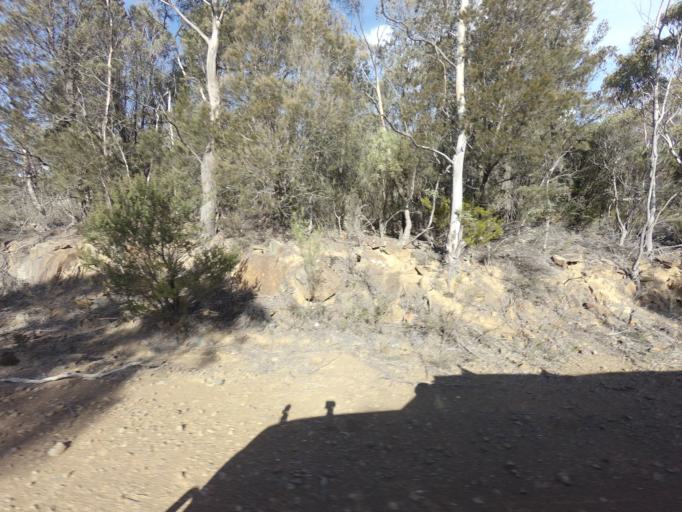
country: AU
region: Tasmania
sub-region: Break O'Day
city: St Helens
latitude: -41.8583
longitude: 148.0241
